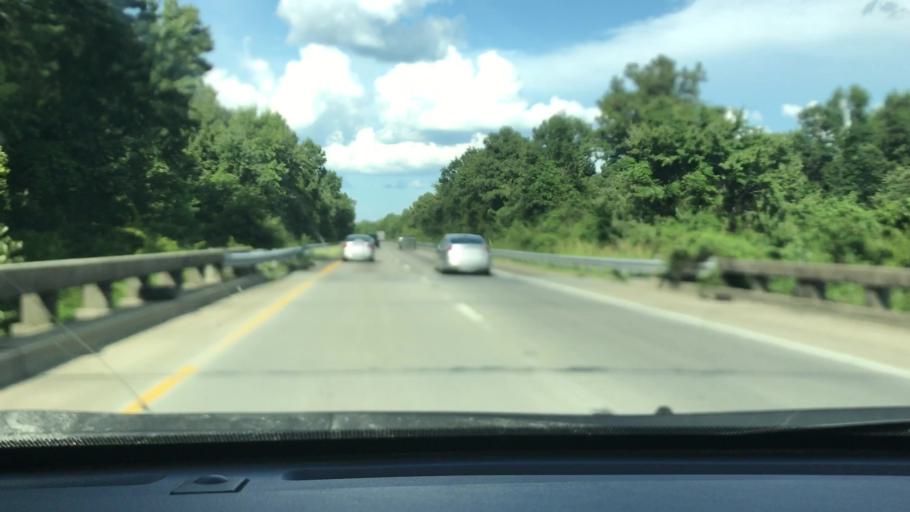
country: US
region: South Carolina
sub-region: Florence County
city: Florence
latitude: 34.2877
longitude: -79.6601
